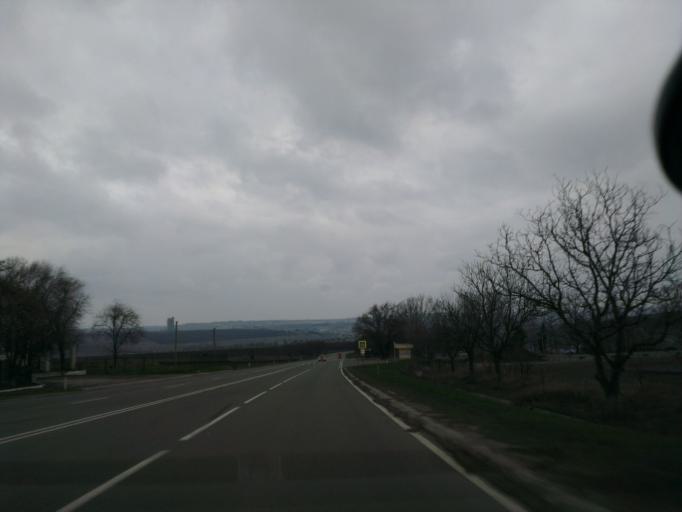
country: MD
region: Laloveni
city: Ialoveni
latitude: 46.9485
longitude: 28.7177
